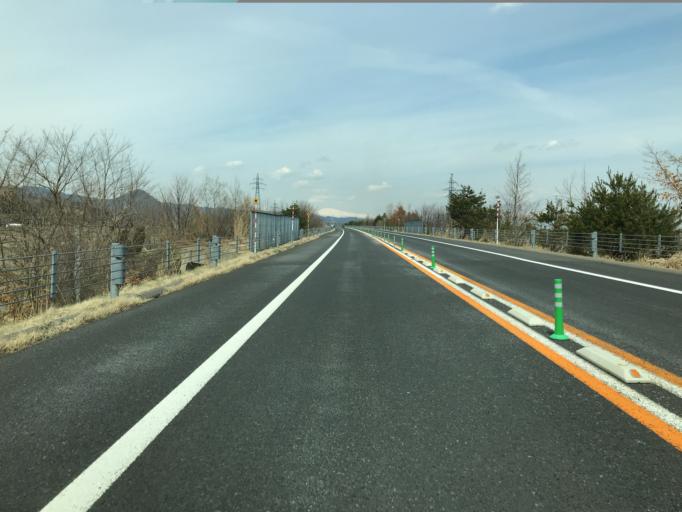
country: JP
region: Yamagata
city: Kaminoyama
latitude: 38.2098
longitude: 140.2923
